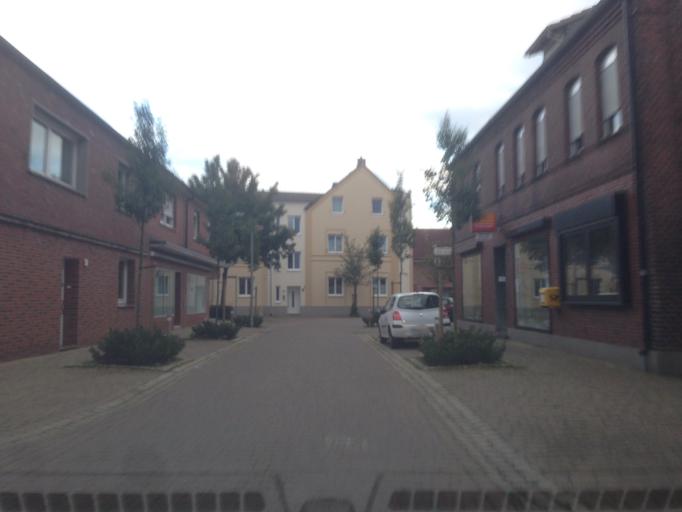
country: DE
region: North Rhine-Westphalia
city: Olfen
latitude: 51.7129
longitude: 7.3770
